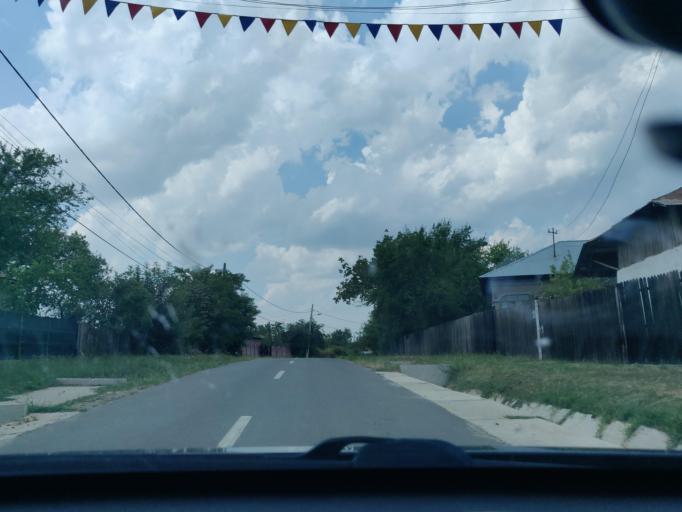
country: RO
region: Teleorman
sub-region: Comuna Sarbeni
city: Sarbeni
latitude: 44.4756
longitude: 25.3852
